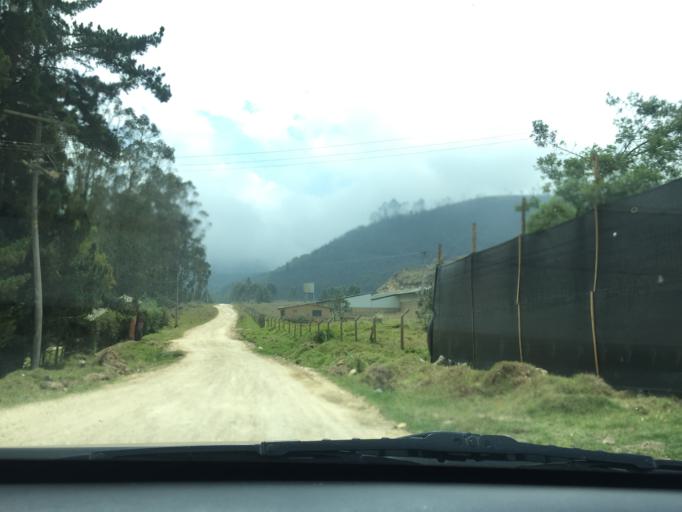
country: CO
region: Cundinamarca
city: Bojaca
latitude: 4.6955
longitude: -74.3137
